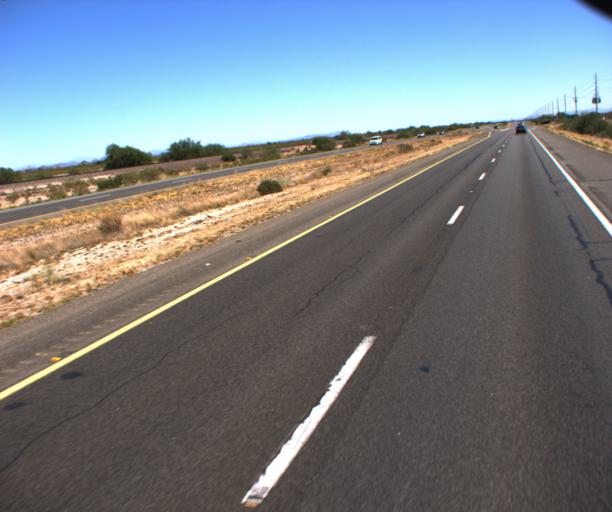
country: US
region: Arizona
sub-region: Maricopa County
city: Sun City West
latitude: 33.7426
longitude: -112.4836
